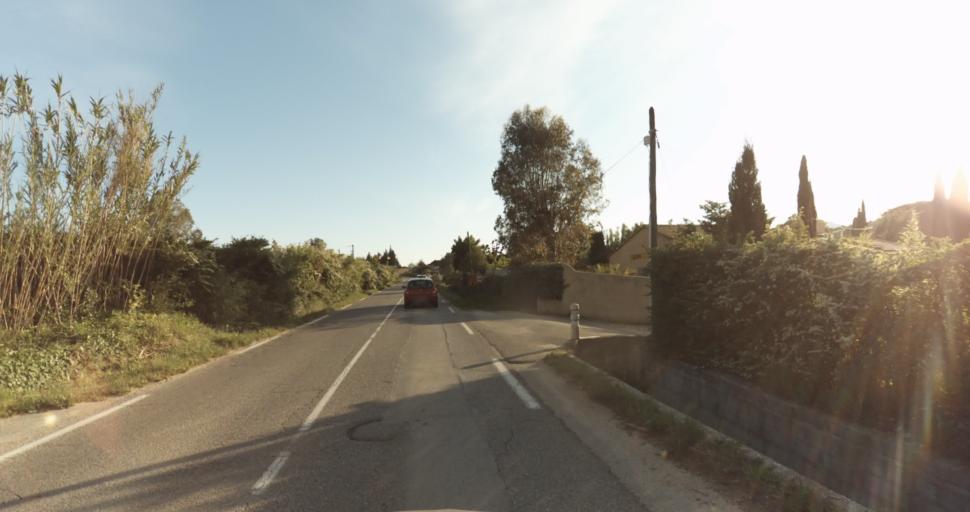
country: FR
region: Provence-Alpes-Cote d'Azur
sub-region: Departement du Var
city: La Crau
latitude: 43.1633
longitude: 6.1015
